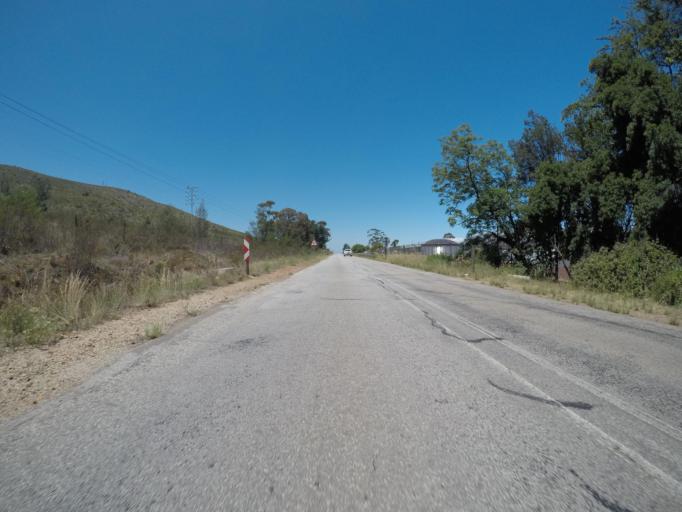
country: ZA
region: Eastern Cape
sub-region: Cacadu District Municipality
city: Kareedouw
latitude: -33.8237
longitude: 23.8642
